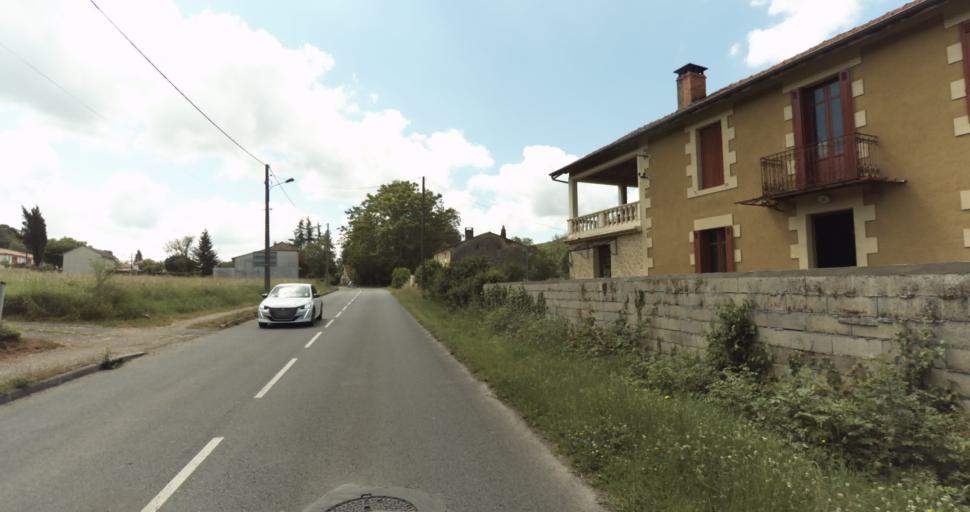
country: FR
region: Aquitaine
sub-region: Departement de la Dordogne
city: Lalinde
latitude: 44.8218
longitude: 0.7064
